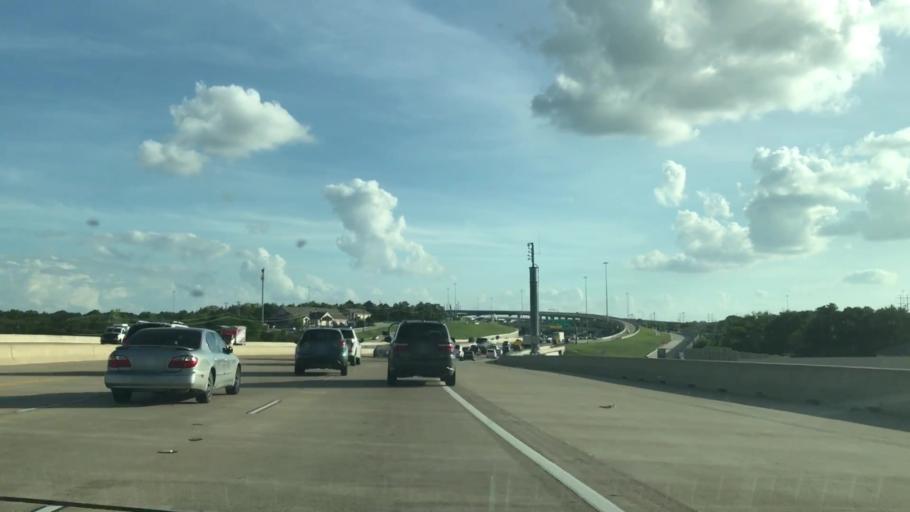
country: US
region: Texas
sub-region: Dallas County
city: Grand Prairie
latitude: 32.7715
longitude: -97.0277
